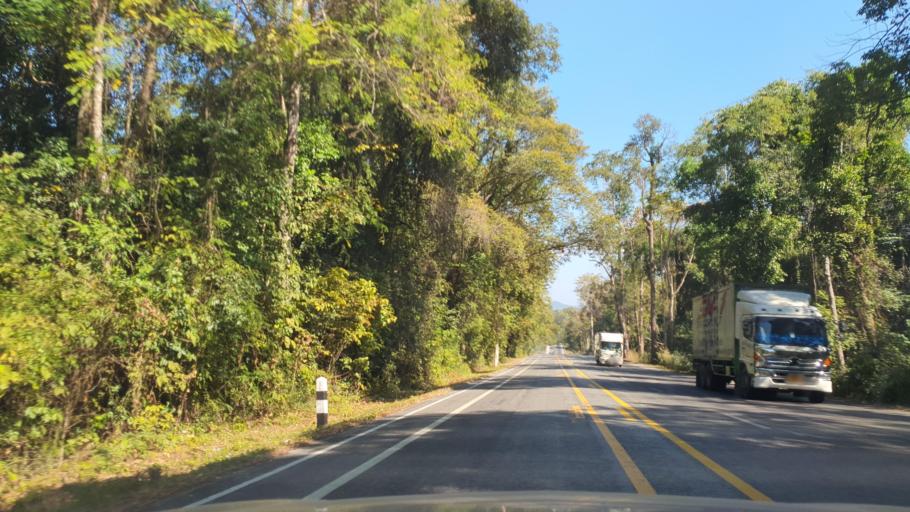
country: TH
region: Kalasin
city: Na Khu
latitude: 16.8466
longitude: 103.9185
